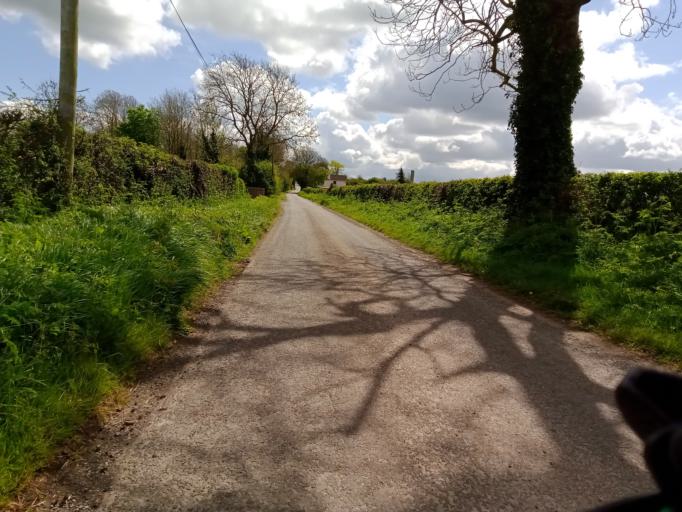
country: IE
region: Leinster
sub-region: Kilkenny
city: Thomastown
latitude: 52.5837
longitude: -7.1360
